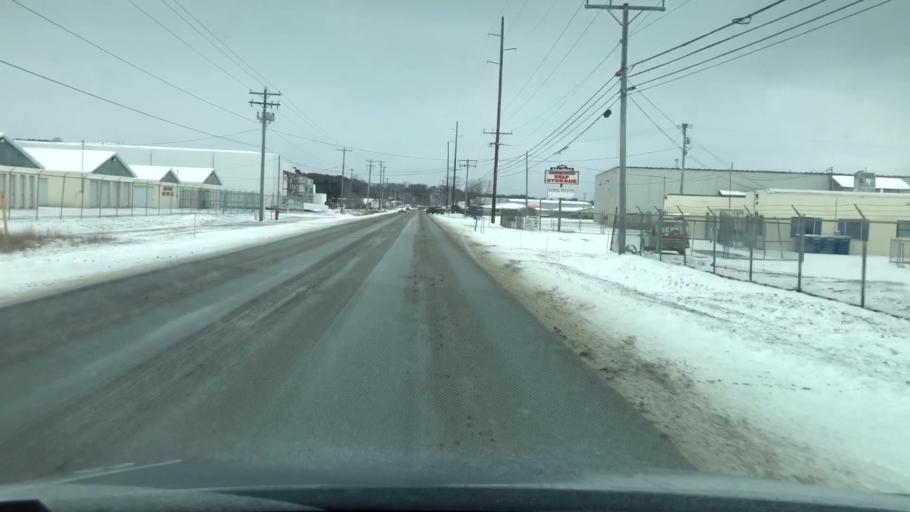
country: US
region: Michigan
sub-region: Grand Traverse County
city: Traverse City
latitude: 44.7240
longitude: -85.6258
